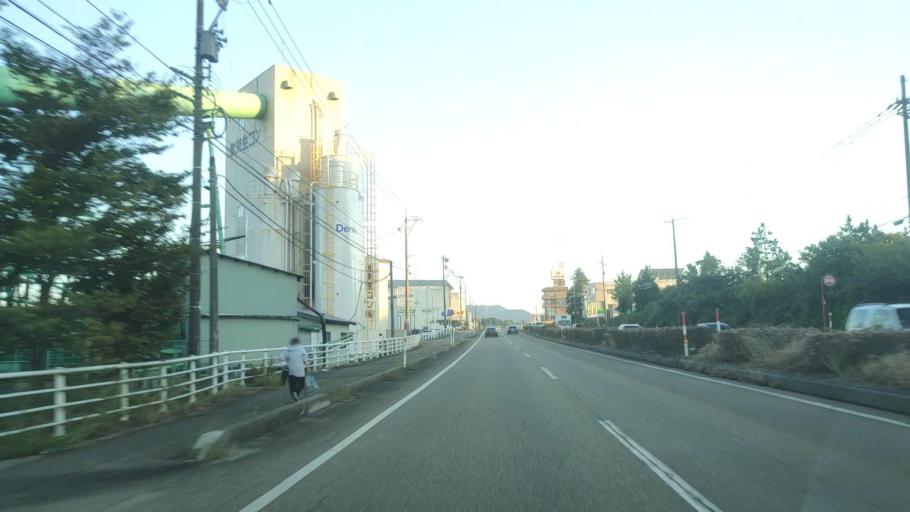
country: JP
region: Toyama
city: Himi
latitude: 36.8306
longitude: 136.9922
